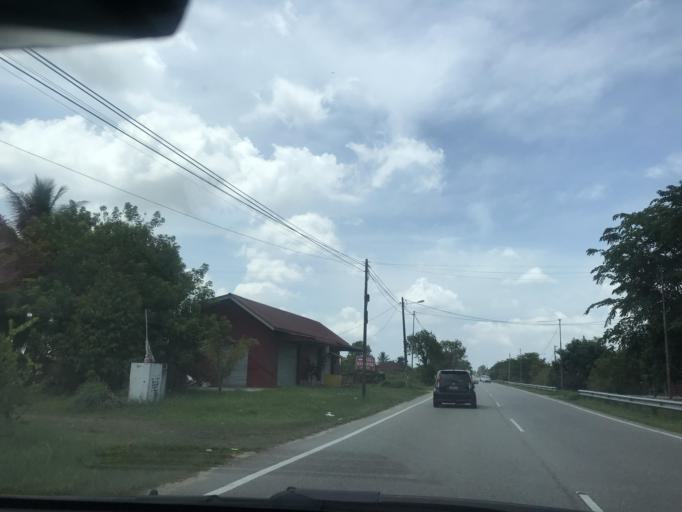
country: MY
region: Kelantan
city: Kota Bharu
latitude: 6.1508
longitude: 102.2103
